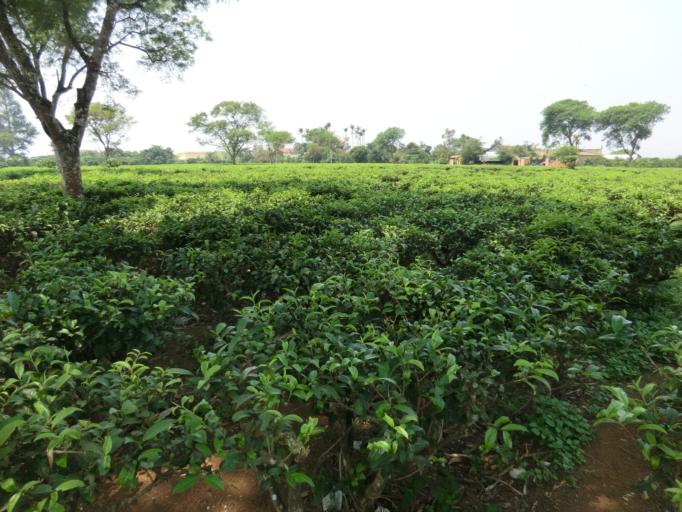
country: VN
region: Lam Dong
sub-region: Thanh Pho Bao Loc
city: Bao Loc
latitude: 11.5467
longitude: 107.7981
